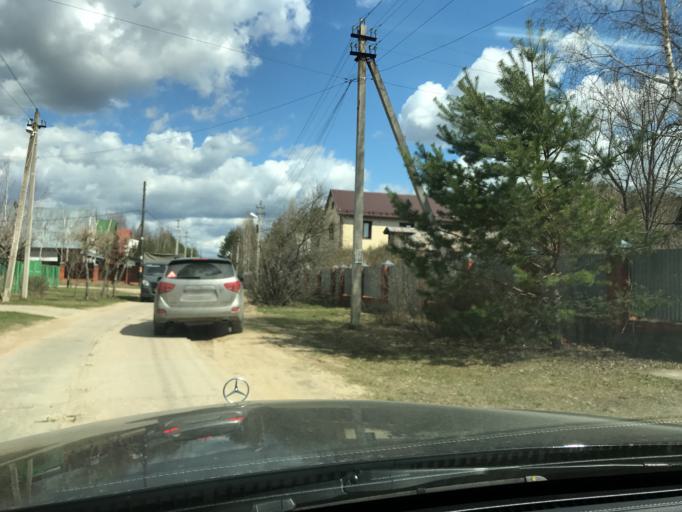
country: RU
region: Vladimir
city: Pokrov
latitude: 55.8571
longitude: 39.2017
